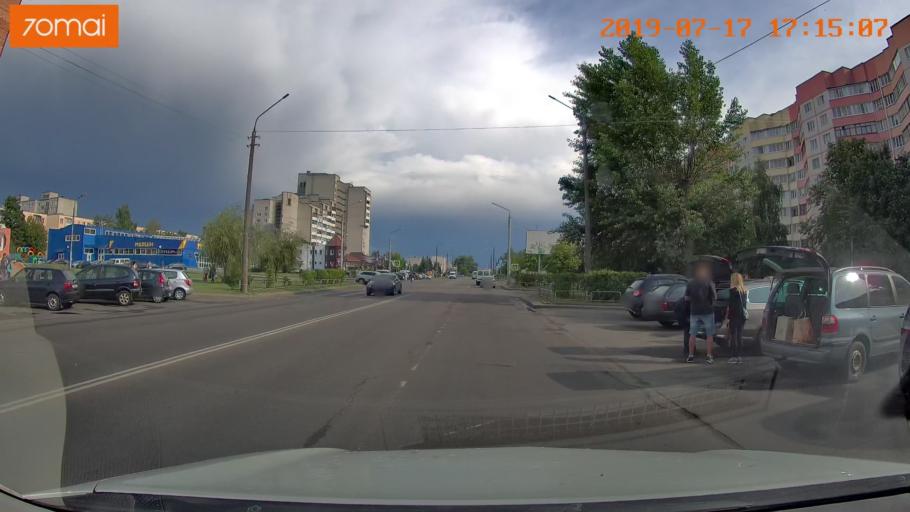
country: BY
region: Mogilev
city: Babruysk
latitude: 53.1715
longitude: 29.1902
